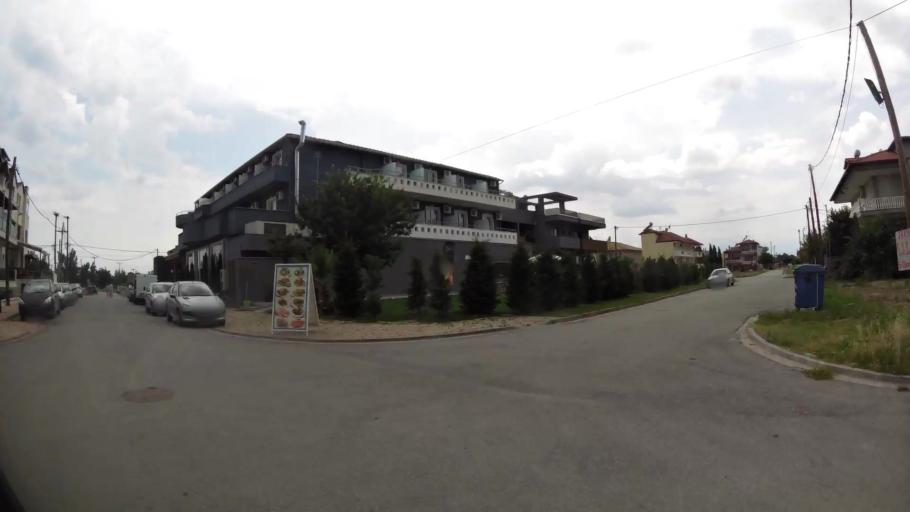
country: GR
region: Central Macedonia
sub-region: Nomos Pierias
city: Paralia
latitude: 40.2766
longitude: 22.5965
